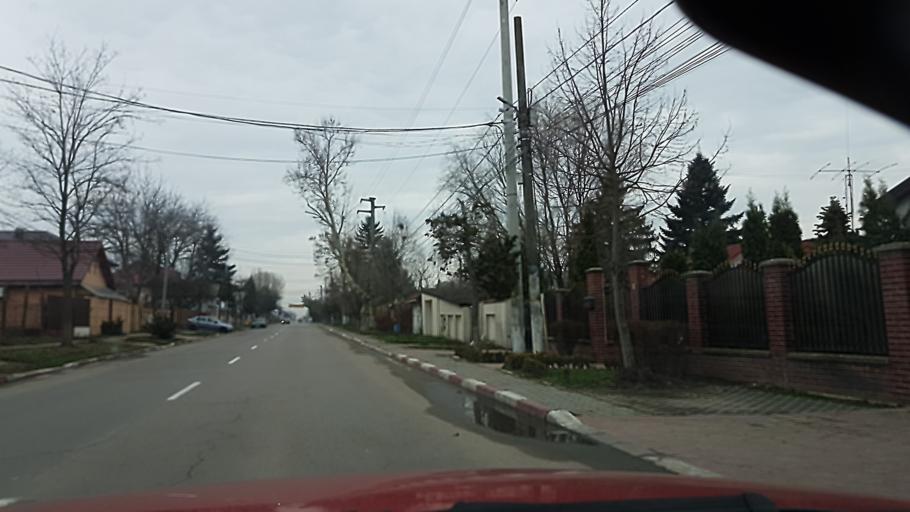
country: RO
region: Ilfov
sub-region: Comuna Corbeanca
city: Corbeanca
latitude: 44.6148
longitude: 26.0816
